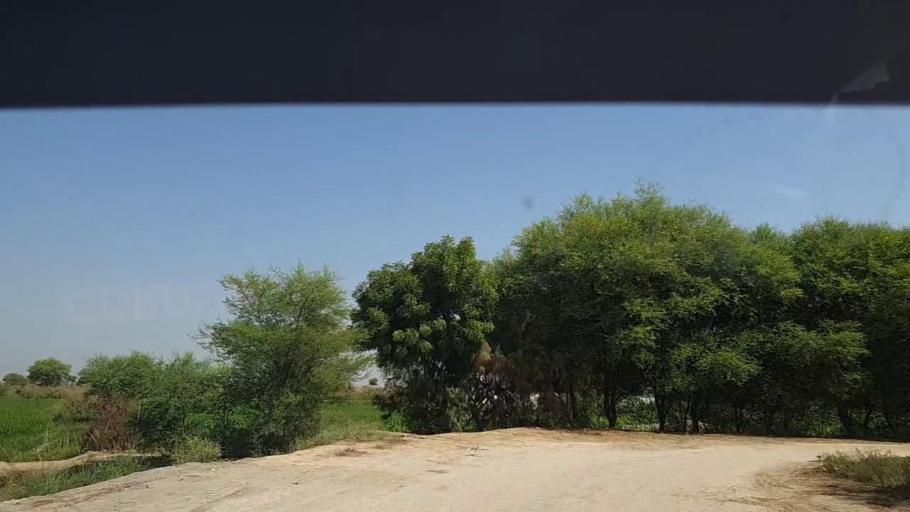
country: PK
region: Sindh
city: Ghauspur
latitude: 28.1563
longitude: 69.1631
